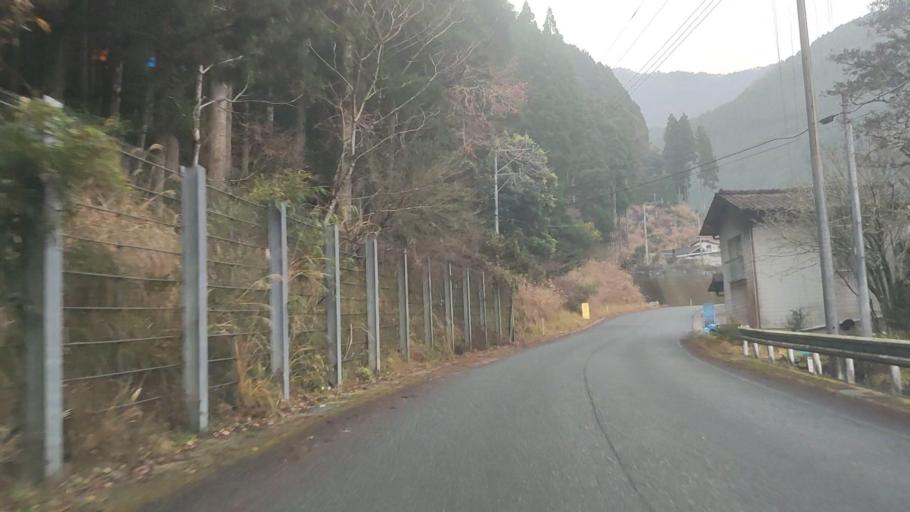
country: JP
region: Kumamoto
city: Matsubase
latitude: 32.5977
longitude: 130.8895
